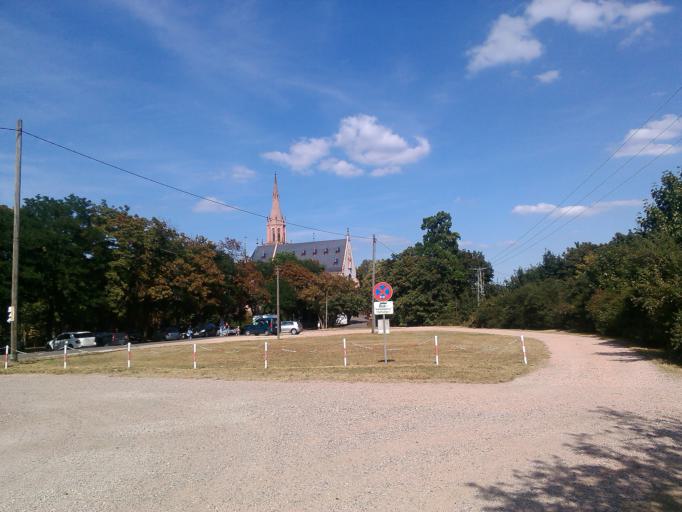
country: DE
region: Hesse
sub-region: Regierungsbezirk Darmstadt
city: Rudesheim am Rhein
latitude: 49.9657
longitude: 7.9244
